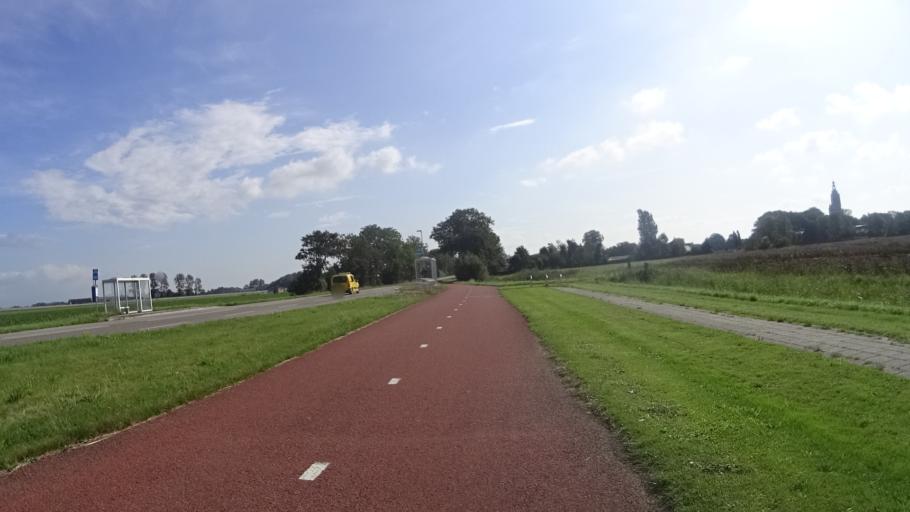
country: NL
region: Friesland
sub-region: Menameradiel
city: Dronryp
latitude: 53.1985
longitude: 5.6374
